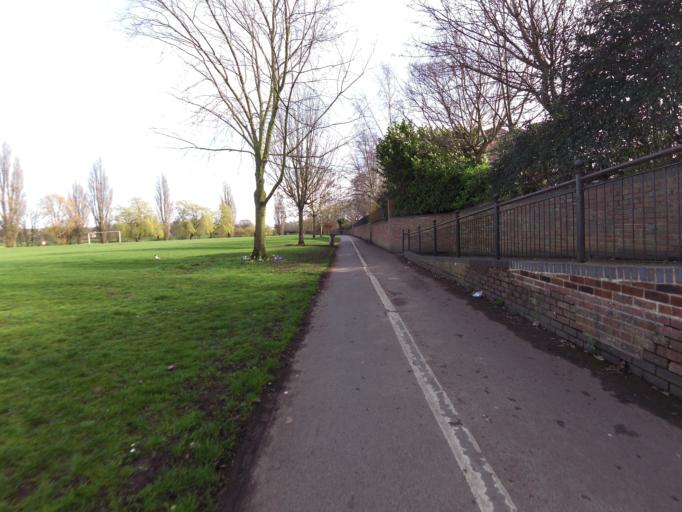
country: GB
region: England
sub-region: City of York
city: York
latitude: 53.9629
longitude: -1.1000
